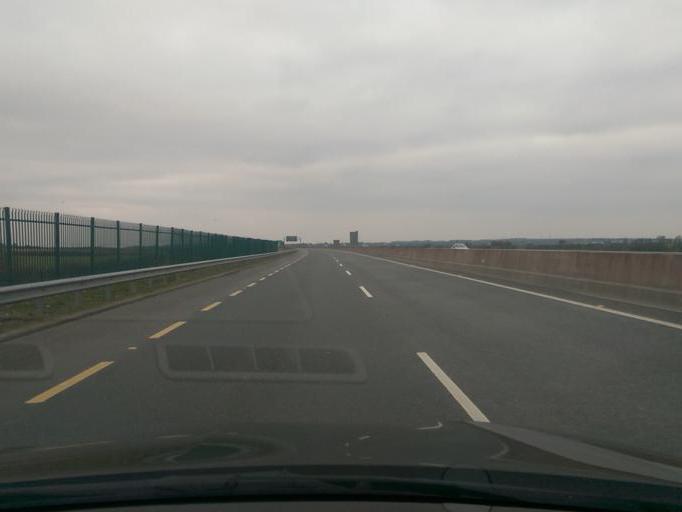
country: IE
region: Connaught
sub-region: County Galway
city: Oranmore
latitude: 53.2949
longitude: -8.9393
